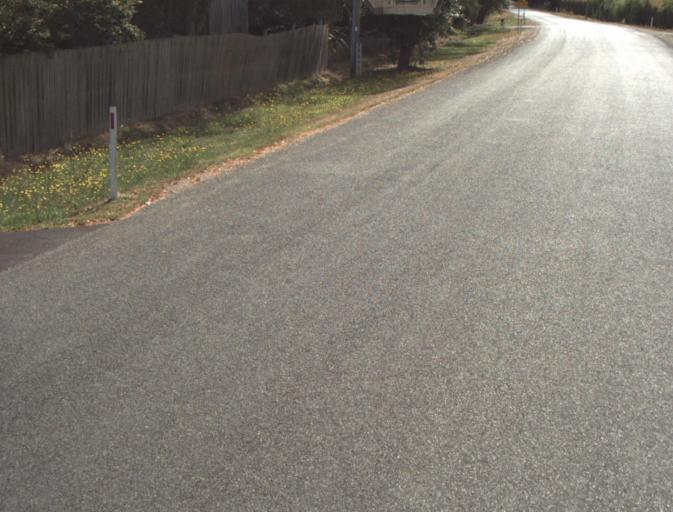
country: AU
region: Tasmania
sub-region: Launceston
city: Mayfield
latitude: -41.2614
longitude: 147.1591
